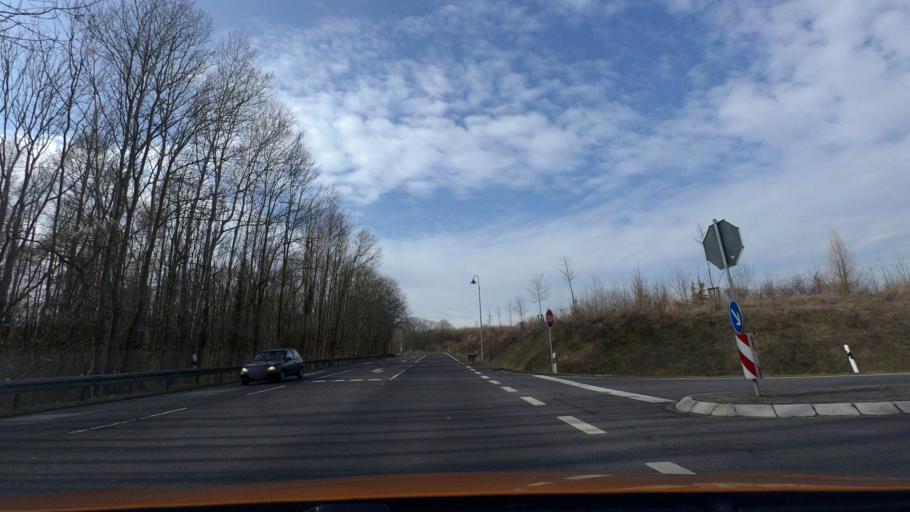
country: DE
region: Saxony-Anhalt
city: Beendorf
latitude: 52.2203
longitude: 11.1017
